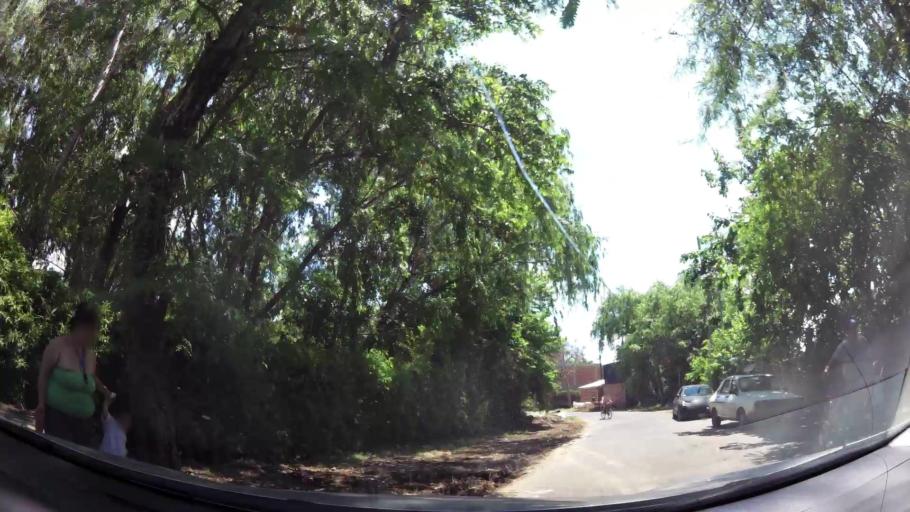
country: AR
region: Buenos Aires
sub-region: Partido de Tigre
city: Tigre
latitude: -34.4259
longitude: -58.5965
